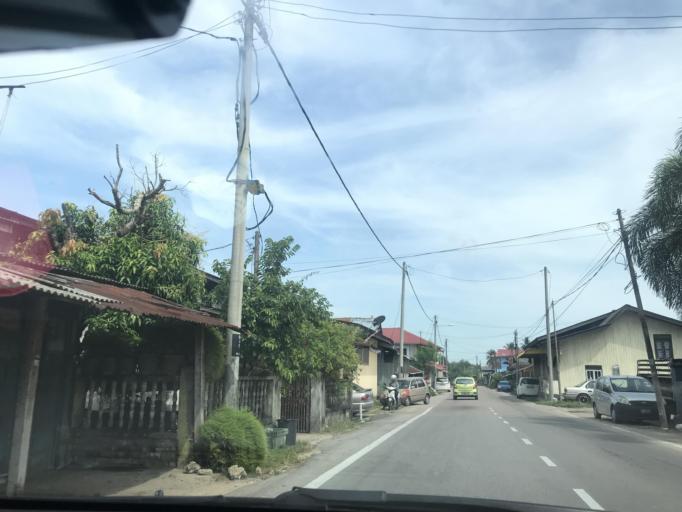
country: MY
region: Kelantan
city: Tumpat
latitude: 6.2001
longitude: 102.1620
